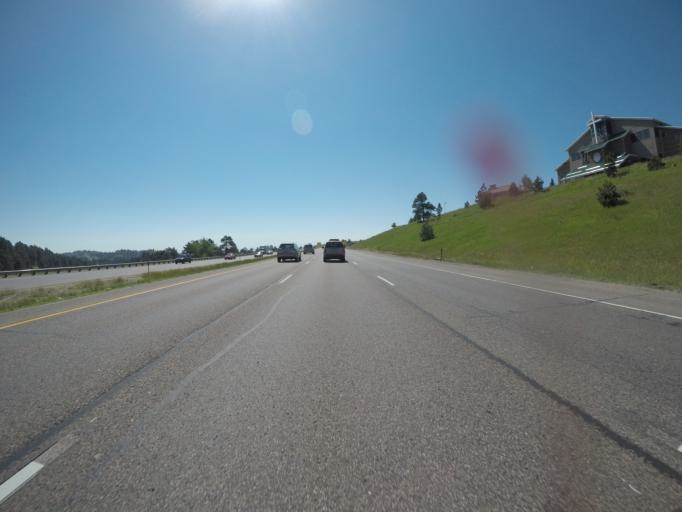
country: US
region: Colorado
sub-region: Jefferson County
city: Genesee
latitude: 39.7079
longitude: -105.2816
